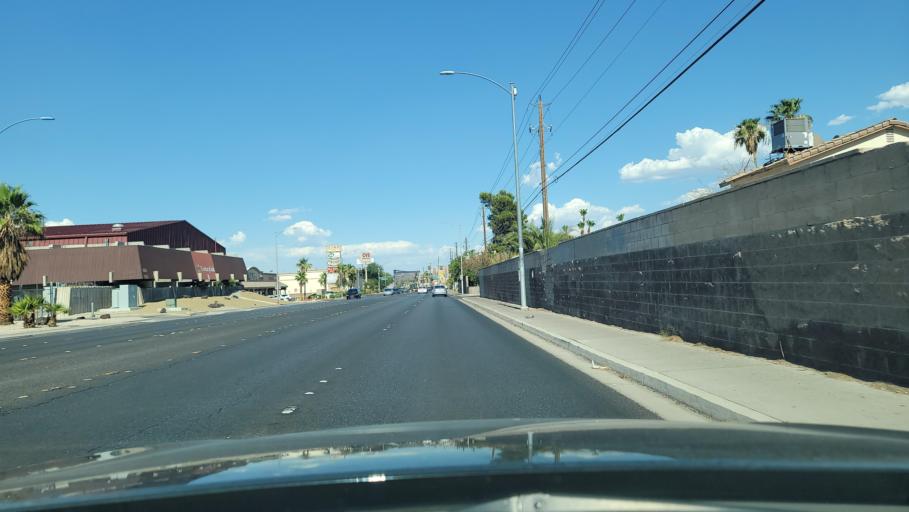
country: US
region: Nevada
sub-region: Clark County
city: Spring Valley
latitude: 36.1254
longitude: -115.2282
